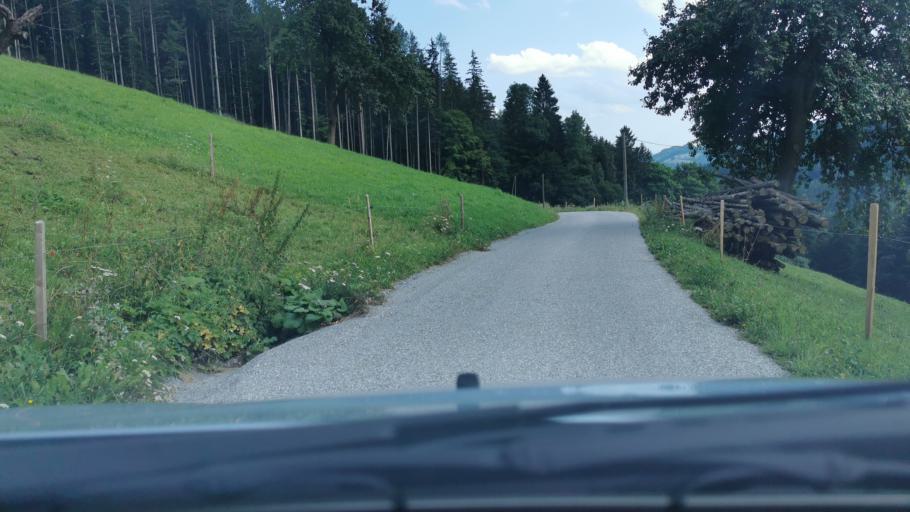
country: AT
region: Styria
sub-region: Politischer Bezirk Weiz
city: Koglhof
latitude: 47.3244
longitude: 15.6650
